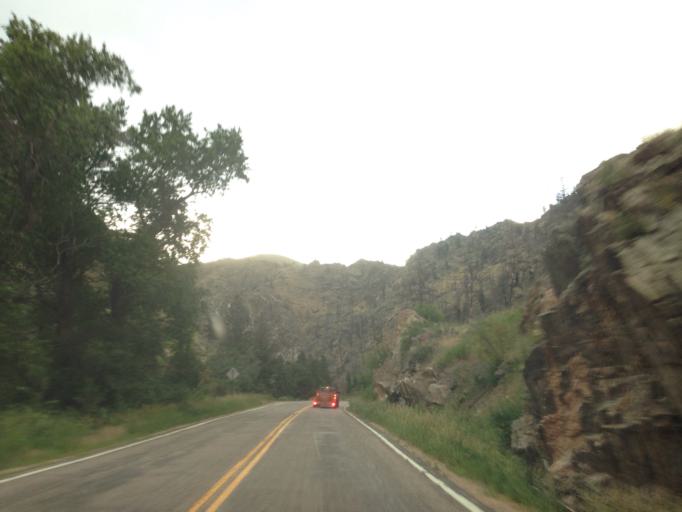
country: US
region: Colorado
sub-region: Larimer County
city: Laporte
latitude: 40.6841
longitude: -105.3801
